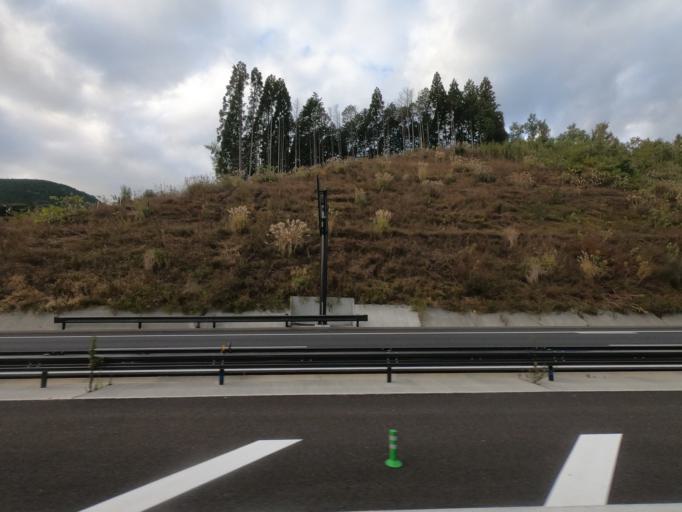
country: JP
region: Kumamoto
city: Minamata
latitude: 32.2409
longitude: 130.4644
